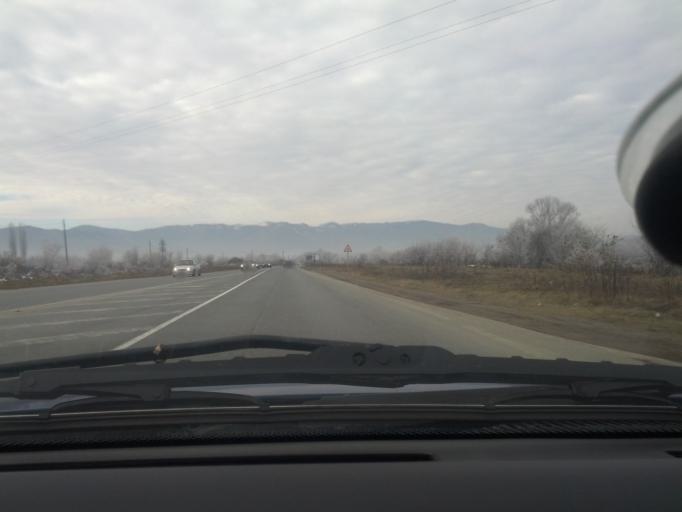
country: BG
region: Sofiya
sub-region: Obshtina Botevgrad
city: Botevgrad
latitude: 42.9254
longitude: 23.7879
